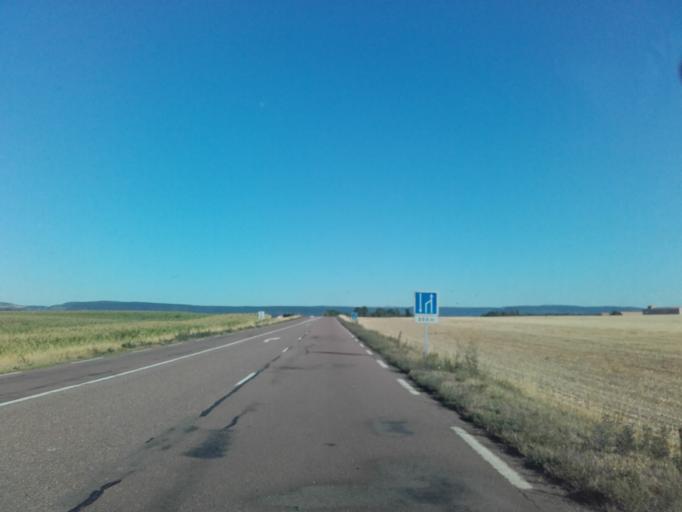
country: FR
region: Bourgogne
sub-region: Departement de Saone-et-Loire
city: Chagny
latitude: 46.8870
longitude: 4.7719
